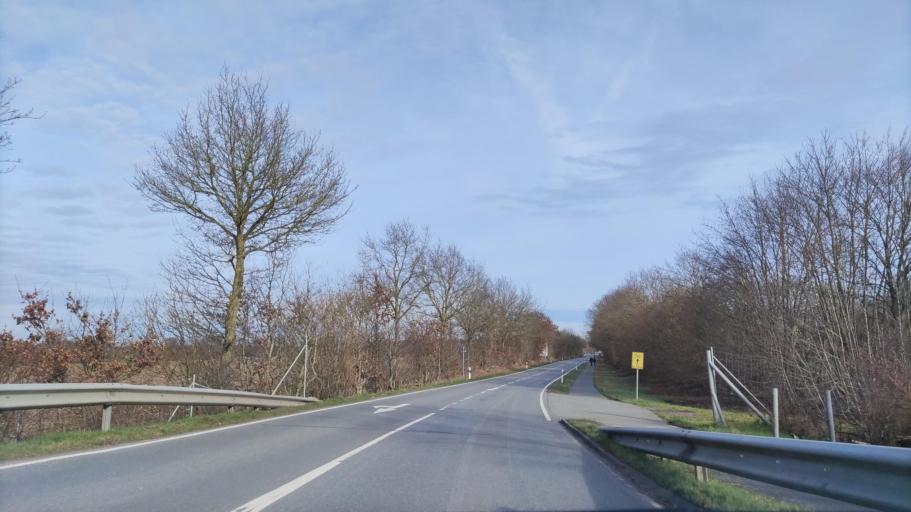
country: DE
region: Schleswig-Holstein
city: Negernbotel
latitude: 53.9748
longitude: 10.2407
